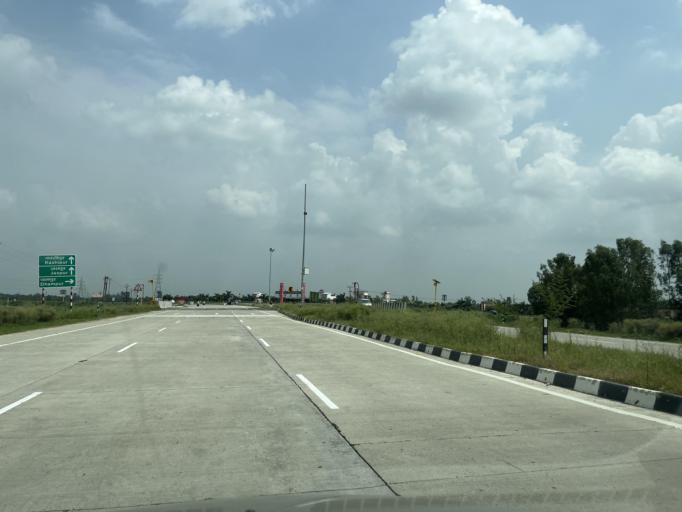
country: IN
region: Uttar Pradesh
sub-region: Bijnor
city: Dhampur
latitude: 29.3170
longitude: 78.5361
